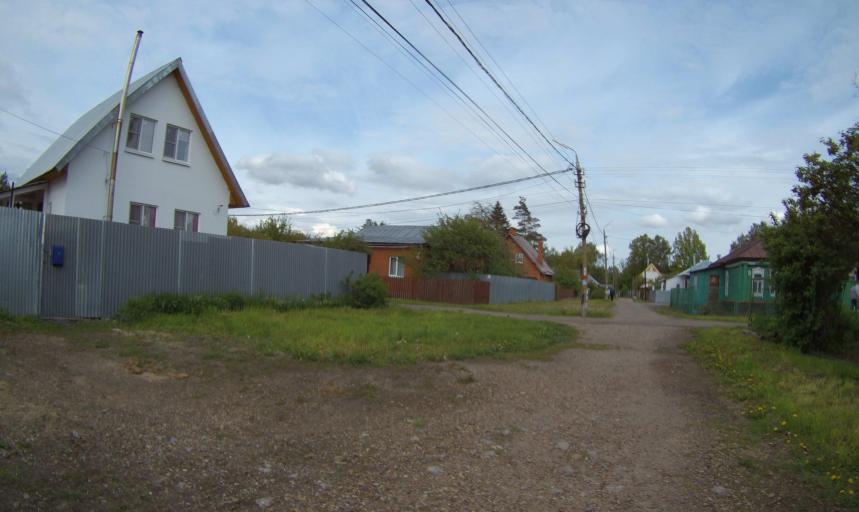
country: RU
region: Moskovskaya
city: Kolomna
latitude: 55.0902
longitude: 38.7873
